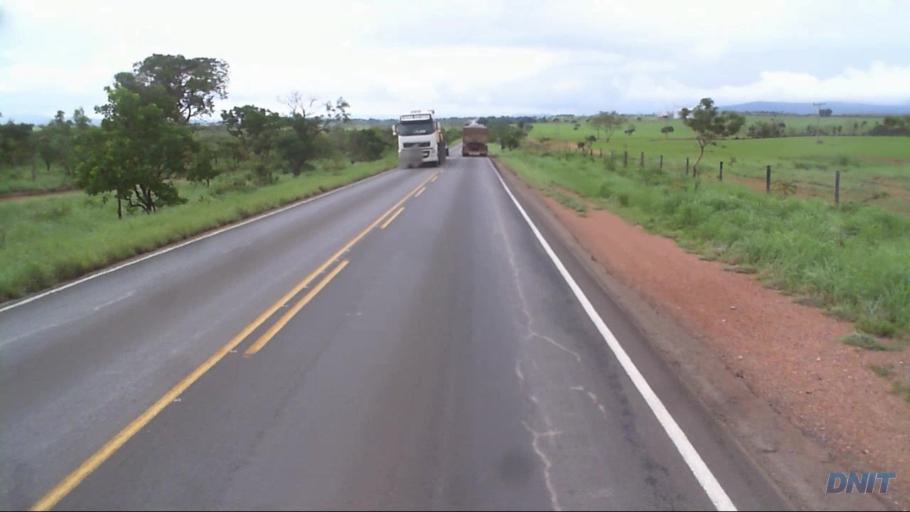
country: BR
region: Goias
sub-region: Padre Bernardo
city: Padre Bernardo
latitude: -15.2278
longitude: -48.2775
